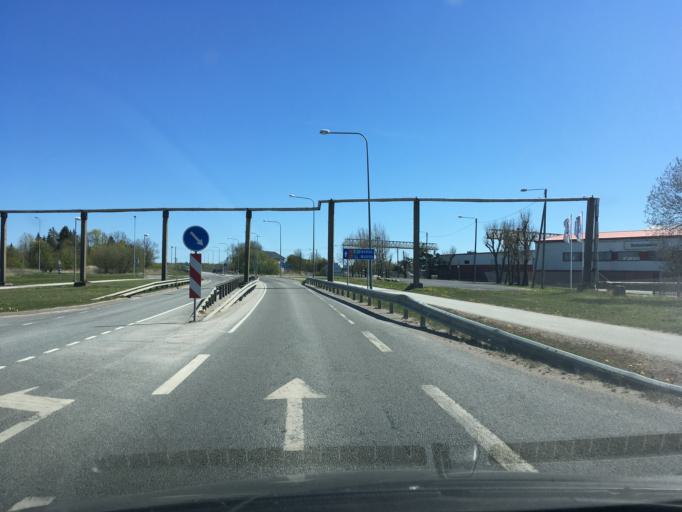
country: EE
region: Harju
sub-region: Joelaehtme vald
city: Loo
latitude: 59.4529
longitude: 24.9668
